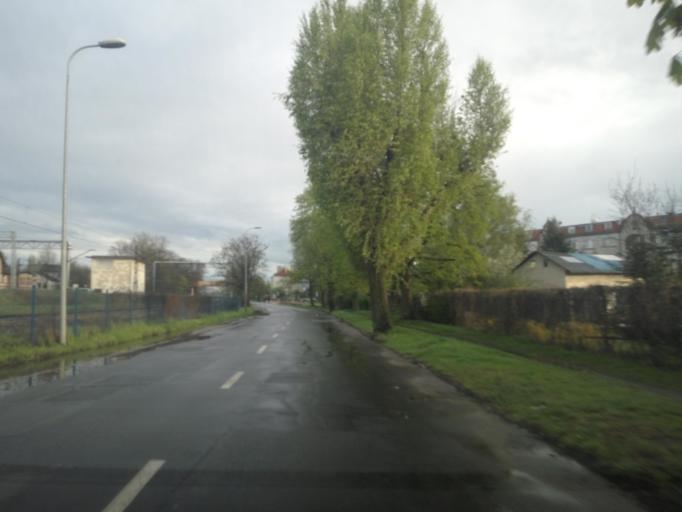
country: PL
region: Lower Silesian Voivodeship
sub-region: Powiat wroclawski
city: Radwanice
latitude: 51.0604
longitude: 17.0860
